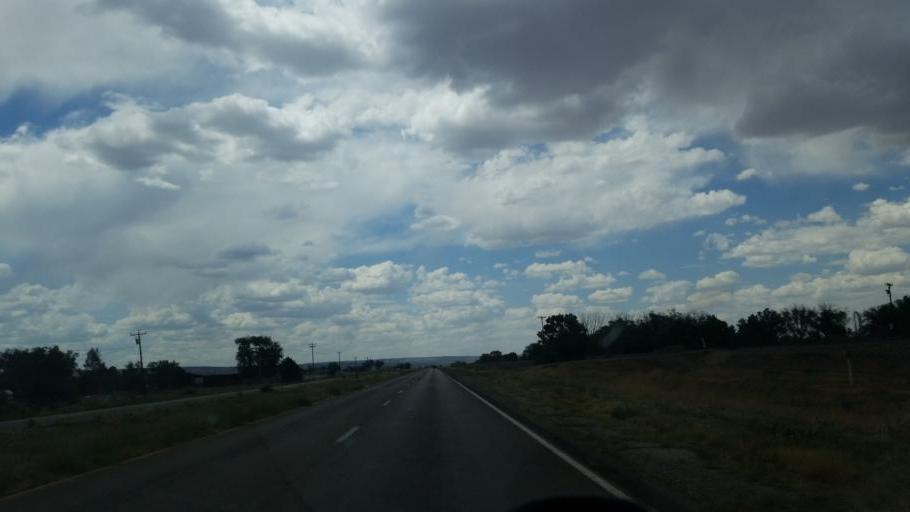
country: US
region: New Mexico
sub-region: Cibola County
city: Milan
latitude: 35.2314
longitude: -107.9304
